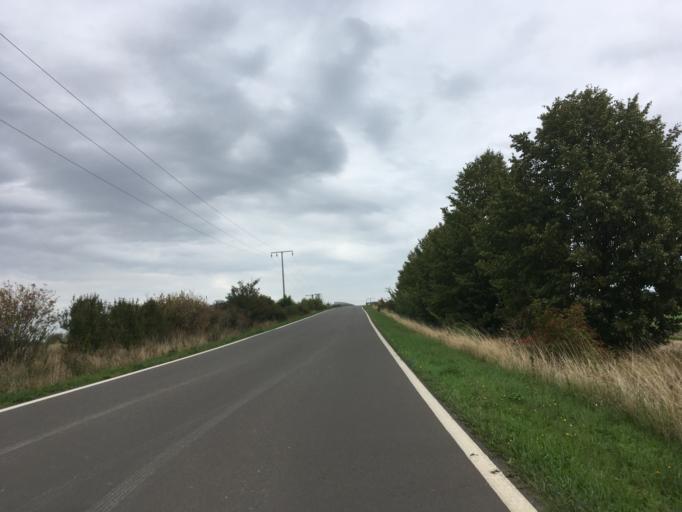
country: DE
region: Brandenburg
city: Pinnow
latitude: 53.0563
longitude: 14.0647
